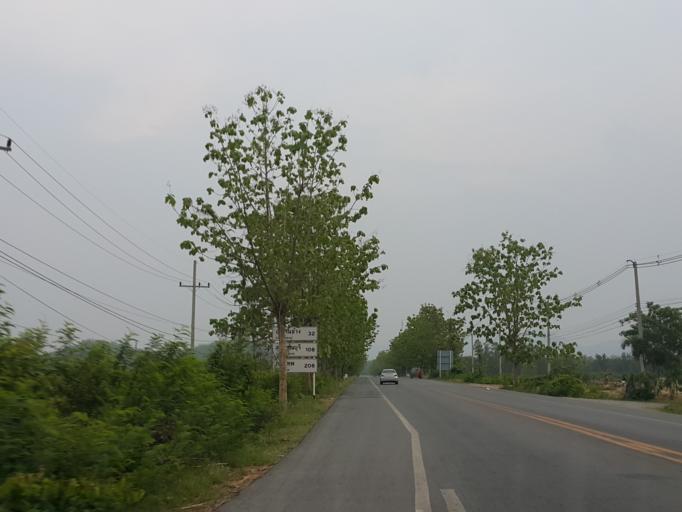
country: TH
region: Uthai Thani
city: Ban Rai
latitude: 15.0842
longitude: 99.5854
